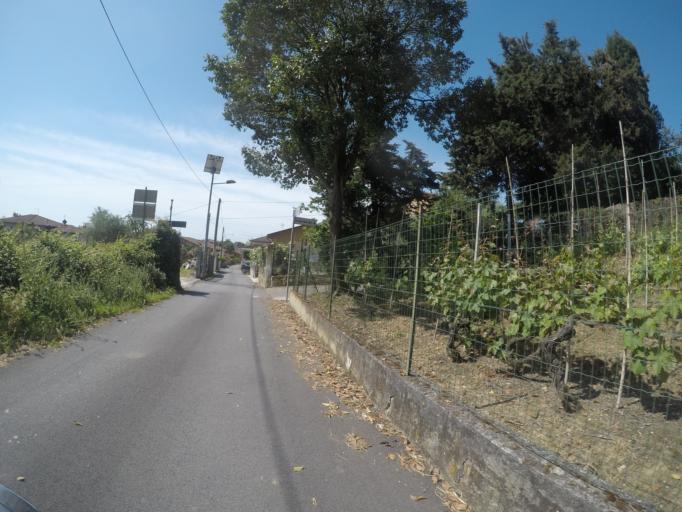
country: IT
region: Tuscany
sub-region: Provincia di Massa-Carrara
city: Carrara
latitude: 44.0442
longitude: 10.0911
